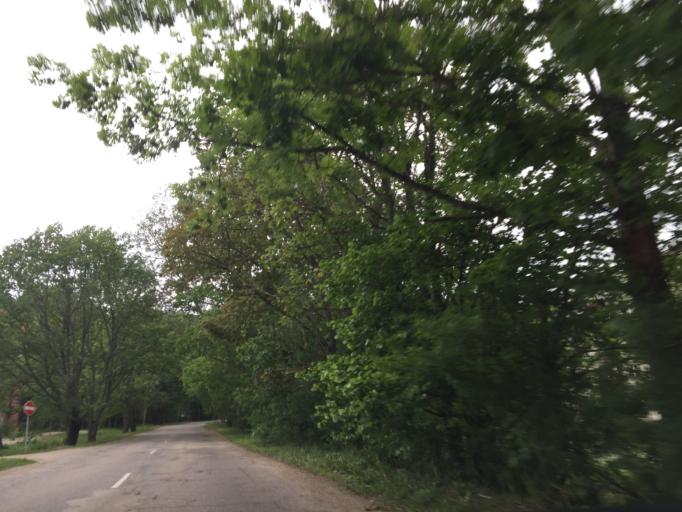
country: LV
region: Preilu Rajons
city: Preili
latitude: 56.0655
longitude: 26.7622
